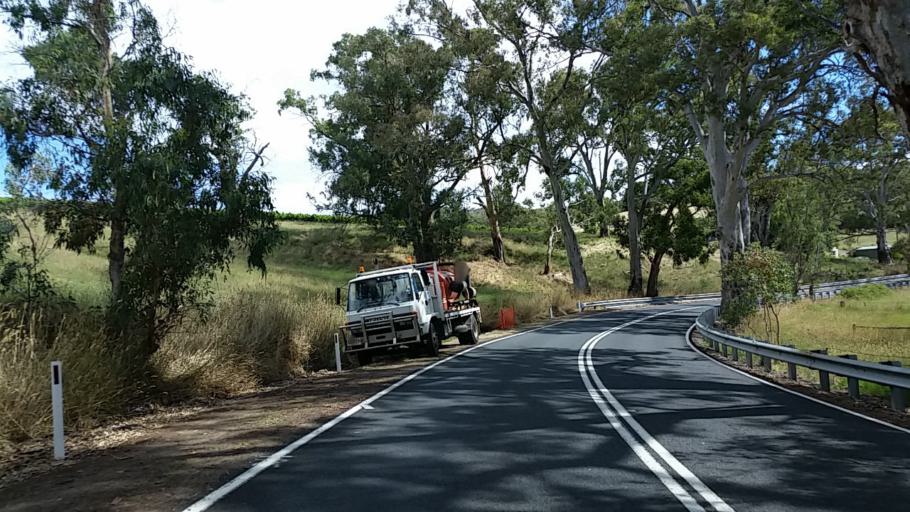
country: AU
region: South Australia
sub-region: Adelaide Hills
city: Gumeracha
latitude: -34.8252
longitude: 138.9232
